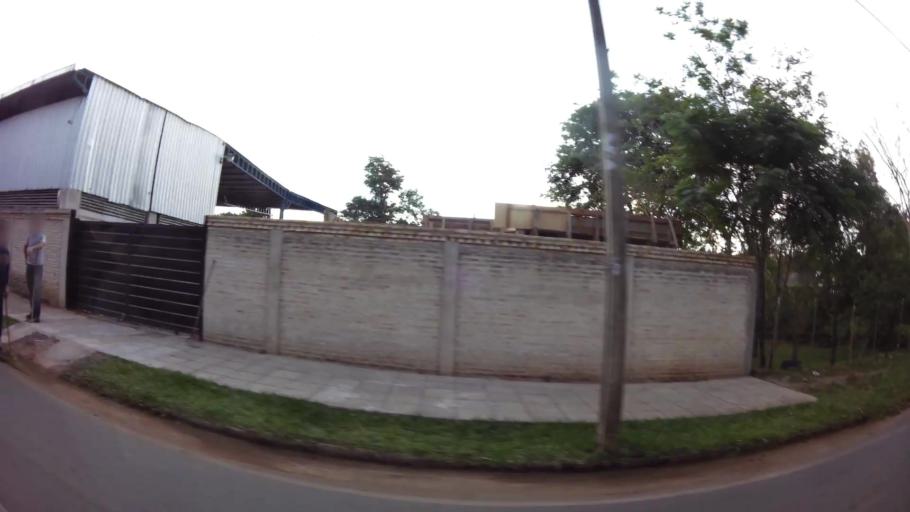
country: PY
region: Central
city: Fernando de la Mora
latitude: -25.3632
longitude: -57.5232
